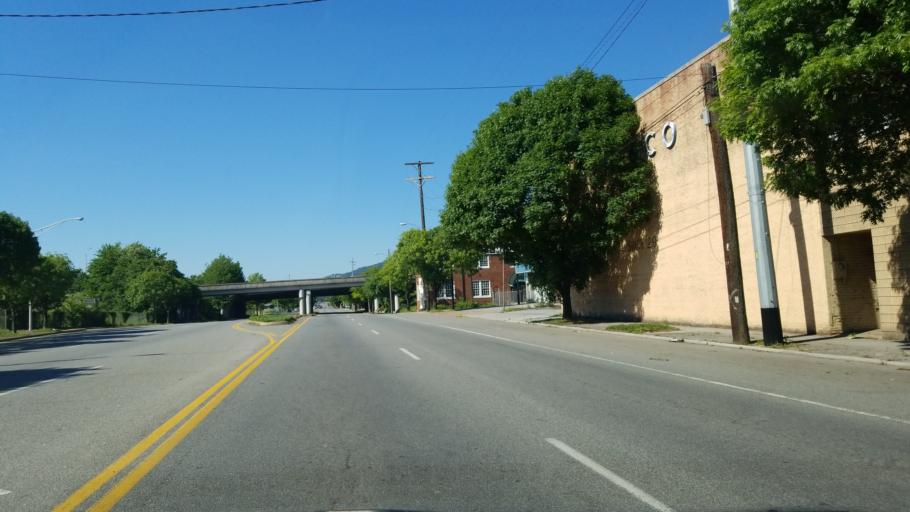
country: US
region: Tennessee
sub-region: Hamilton County
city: Chattanooga
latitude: 35.0325
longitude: -85.3141
